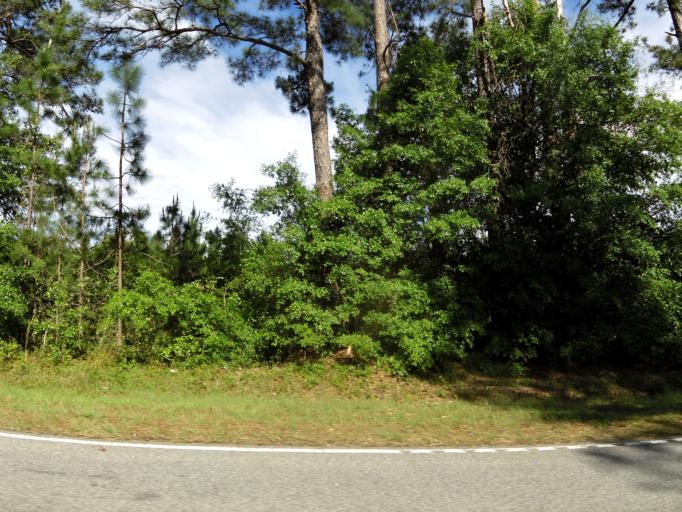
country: US
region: South Carolina
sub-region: Allendale County
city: Allendale
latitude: 33.0935
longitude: -81.2072
